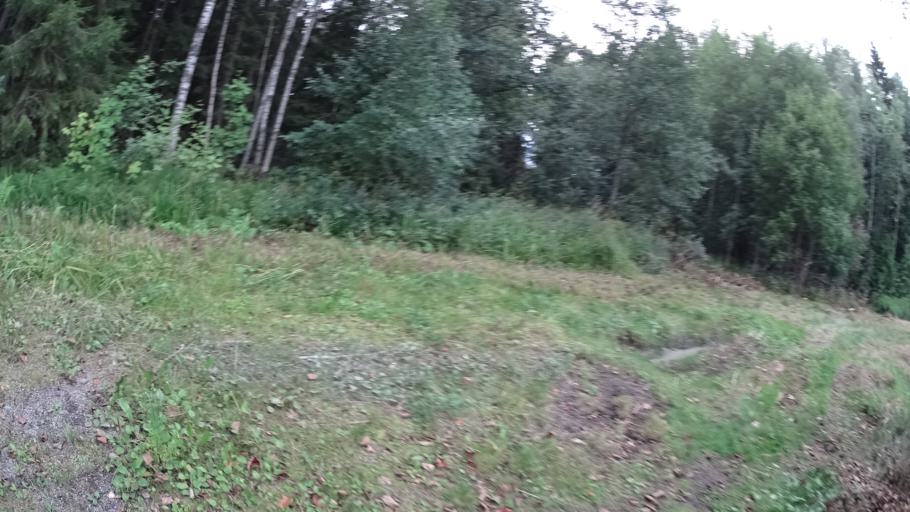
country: FI
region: Uusimaa
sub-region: Helsinki
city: Kilo
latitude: 60.2670
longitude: 24.8303
